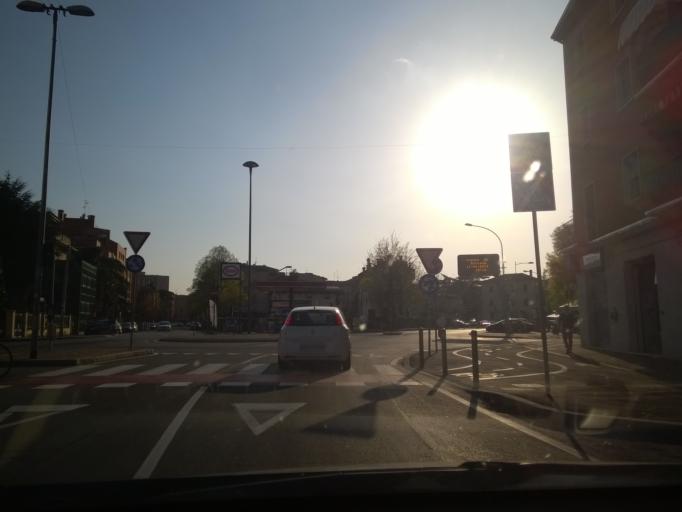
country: IT
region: Emilia-Romagna
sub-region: Provincia di Bologna
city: Bologna
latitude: 44.5038
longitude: 11.3682
